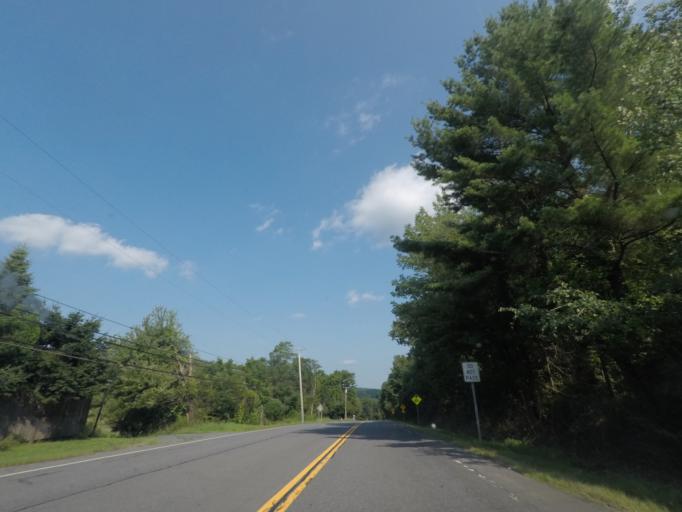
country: US
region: New York
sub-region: Rensselaer County
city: Nassau
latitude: 42.5172
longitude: -73.5760
